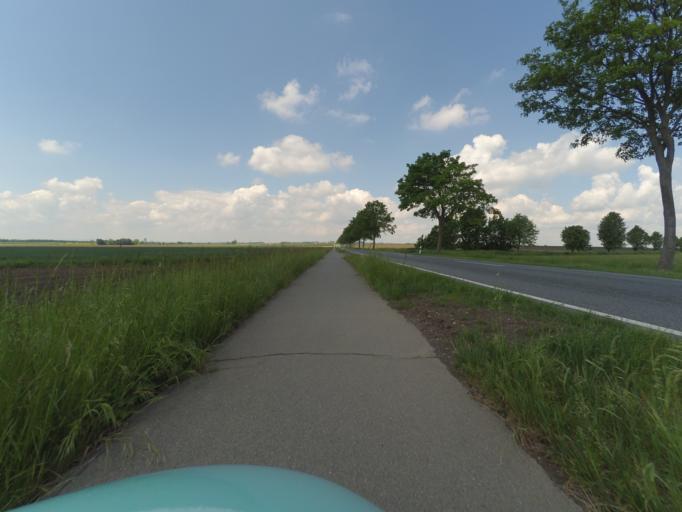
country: DE
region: Lower Saxony
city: Hohenhameln
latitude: 52.2488
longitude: 10.1071
